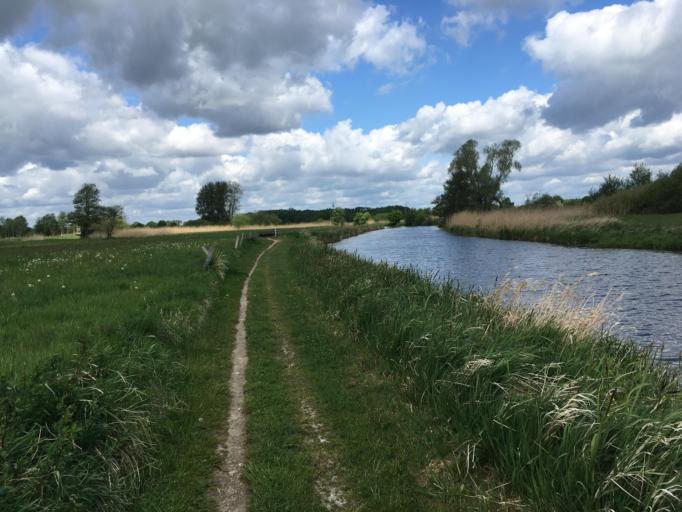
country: DE
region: Lower Saxony
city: Brietlingen
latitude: 53.3335
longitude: 10.4834
